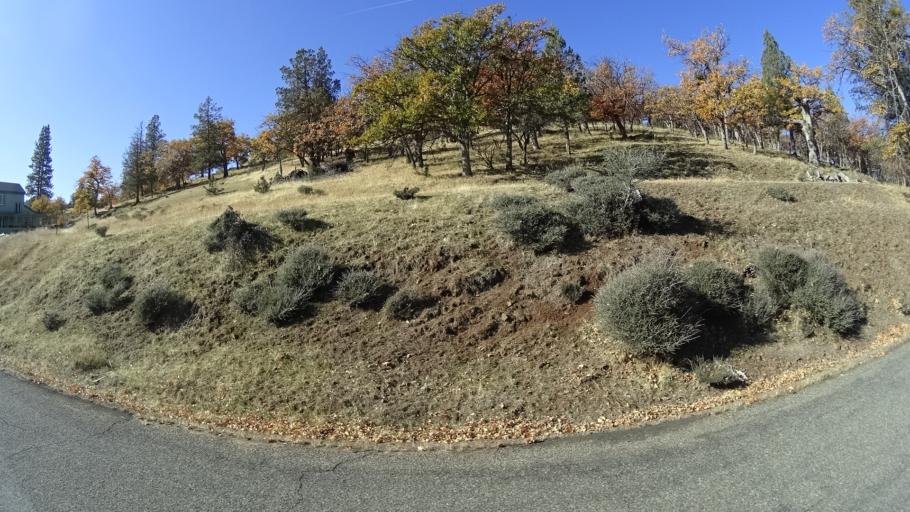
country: US
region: California
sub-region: Siskiyou County
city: Montague
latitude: 41.9755
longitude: -122.3223
